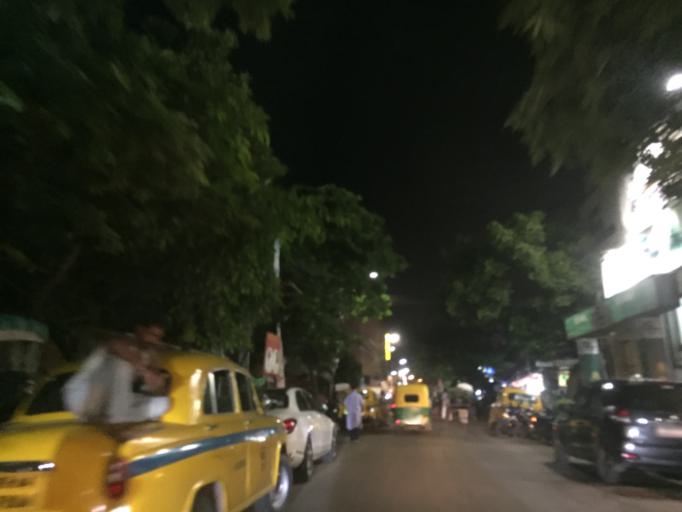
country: IN
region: West Bengal
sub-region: Kolkata
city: Kolkata
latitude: 22.5585
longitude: 88.3549
